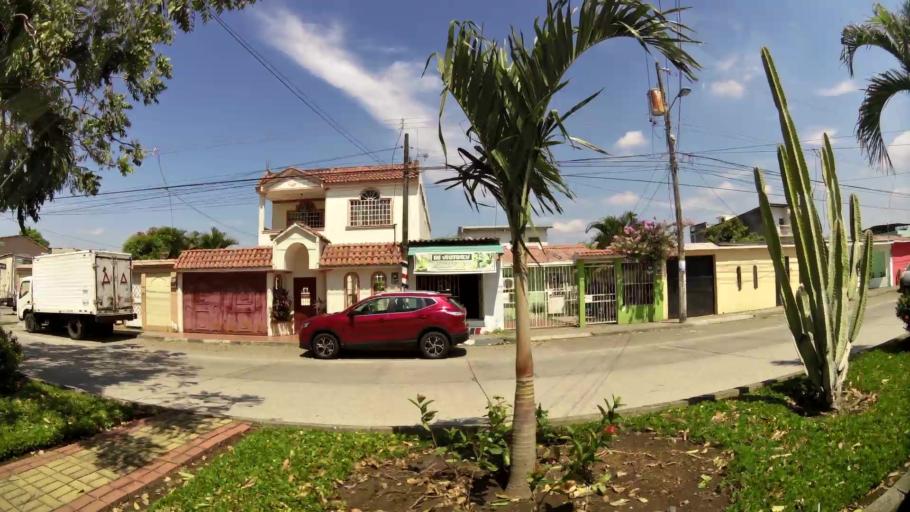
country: EC
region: Guayas
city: Eloy Alfaro
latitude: -2.1102
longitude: -79.8999
